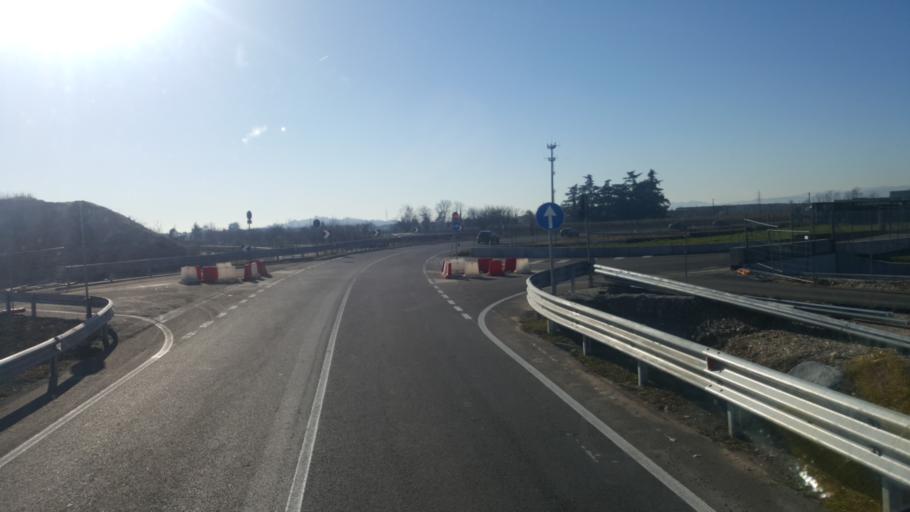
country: IT
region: Veneto
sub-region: Provincia di Vicenza
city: Breganze
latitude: 45.6949
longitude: 11.5690
